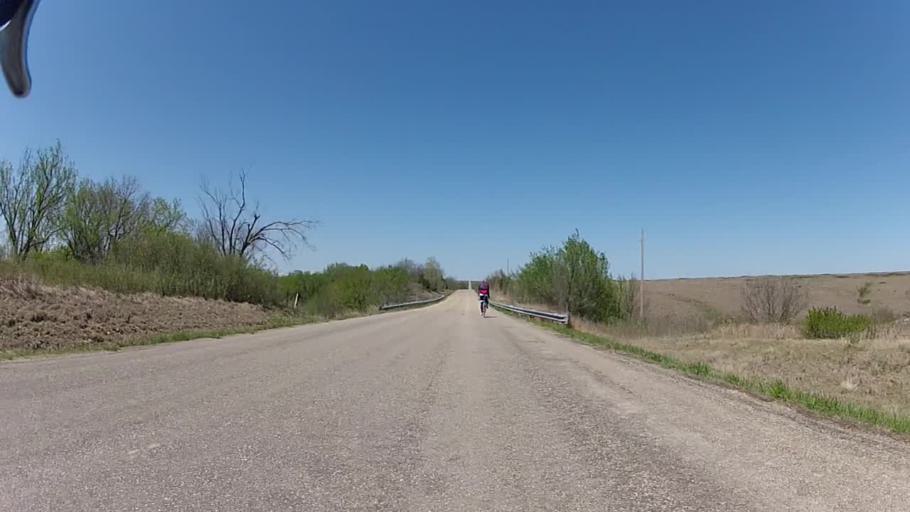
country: US
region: Kansas
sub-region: Riley County
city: Ogden
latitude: 38.9717
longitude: -96.5466
